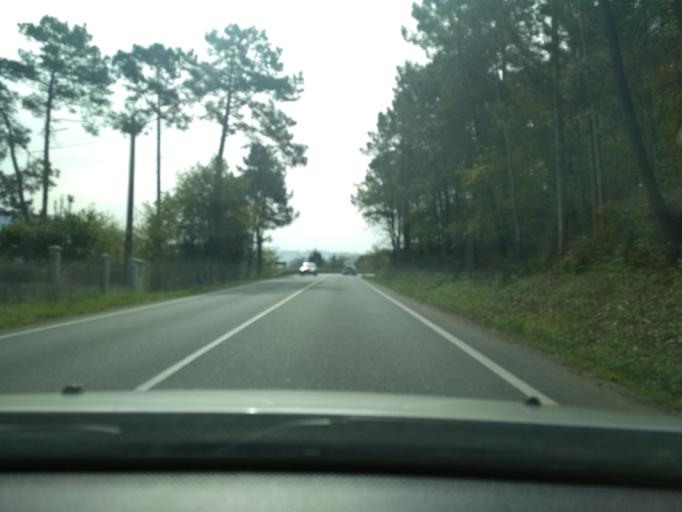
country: ES
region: Galicia
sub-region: Provincia de Pontevedra
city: Catoira
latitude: 42.6757
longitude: -8.7164
